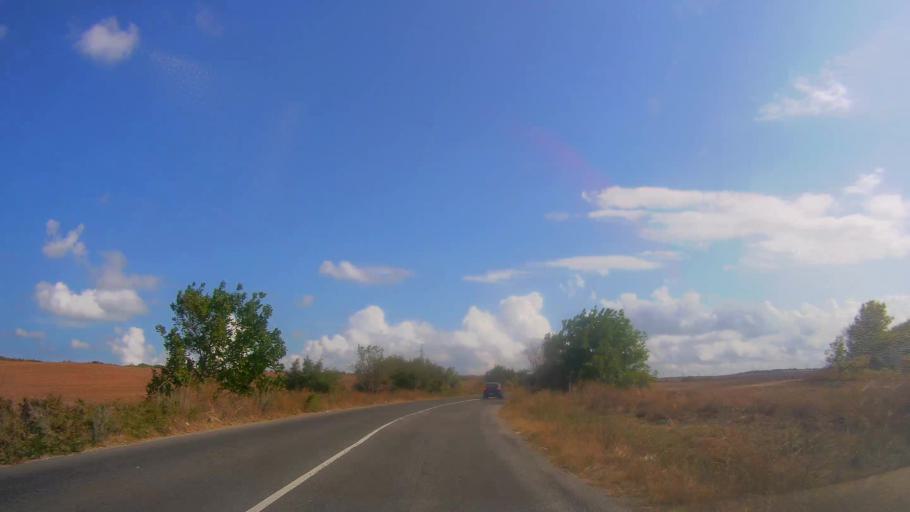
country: BG
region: Burgas
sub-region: Obshtina Burgas
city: Burgas
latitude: 42.4805
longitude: 27.3873
